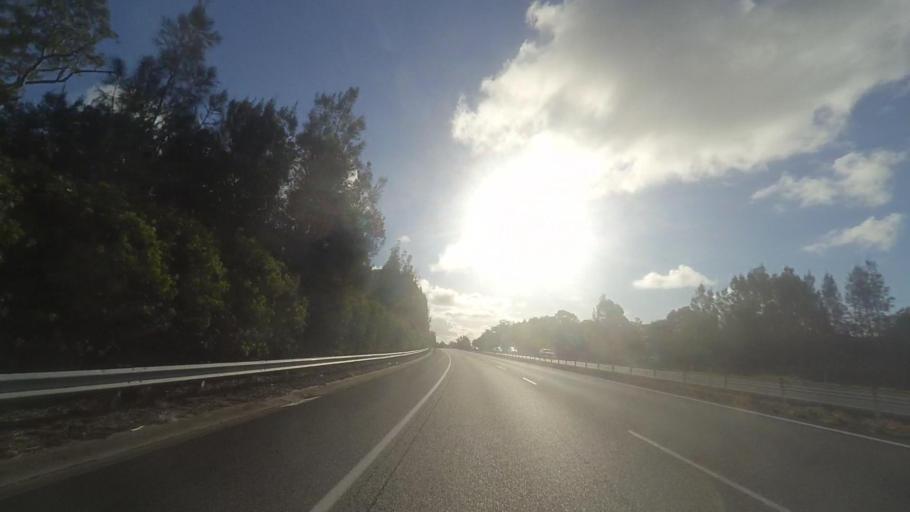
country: AU
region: New South Wales
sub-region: Great Lakes
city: Nabiac
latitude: -32.0927
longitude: 152.3864
